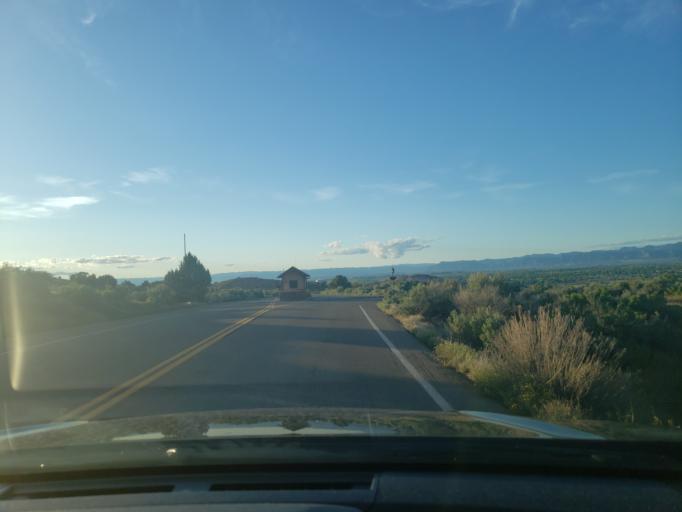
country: US
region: Colorado
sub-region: Mesa County
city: Fruita
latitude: 39.1182
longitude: -108.7312
